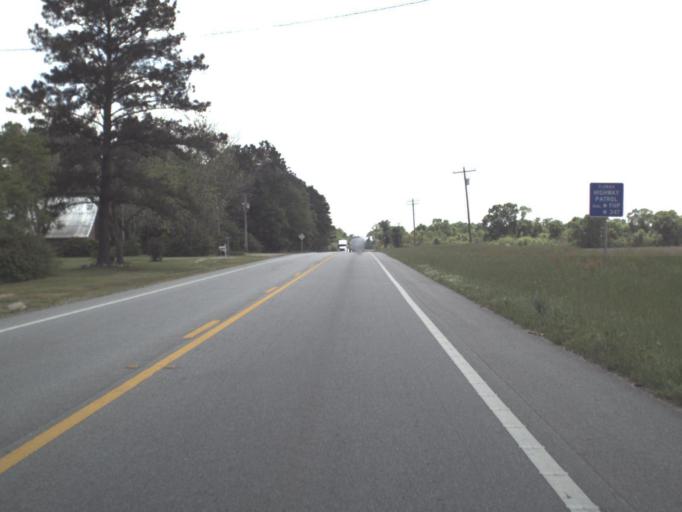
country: US
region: Alabama
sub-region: Escambia County
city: Atmore
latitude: 30.9931
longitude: -87.4897
